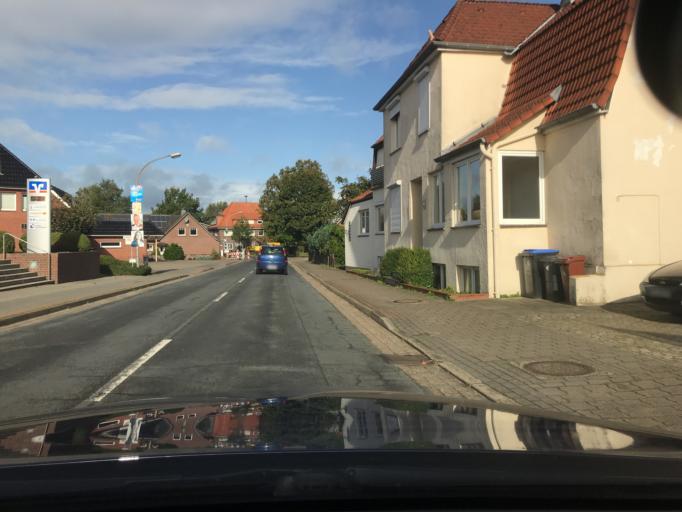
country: DE
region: Lower Saxony
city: Ahlerstedt
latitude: 53.4023
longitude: 9.4517
